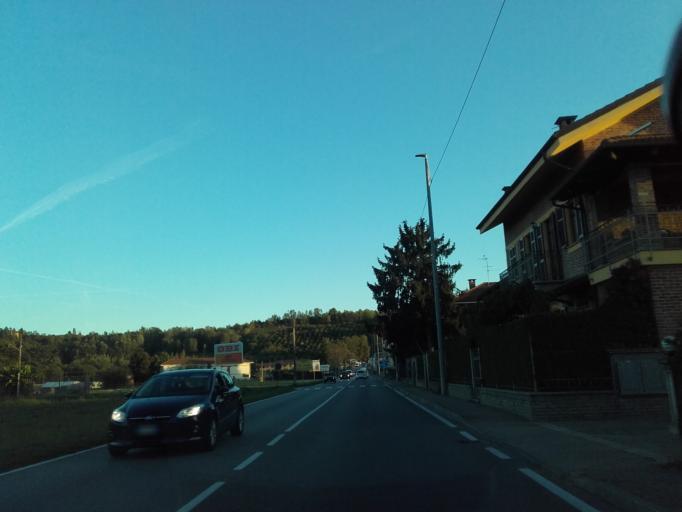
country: IT
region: Piedmont
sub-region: Provincia di Asti
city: Asti
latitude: 44.8796
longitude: 8.2140
